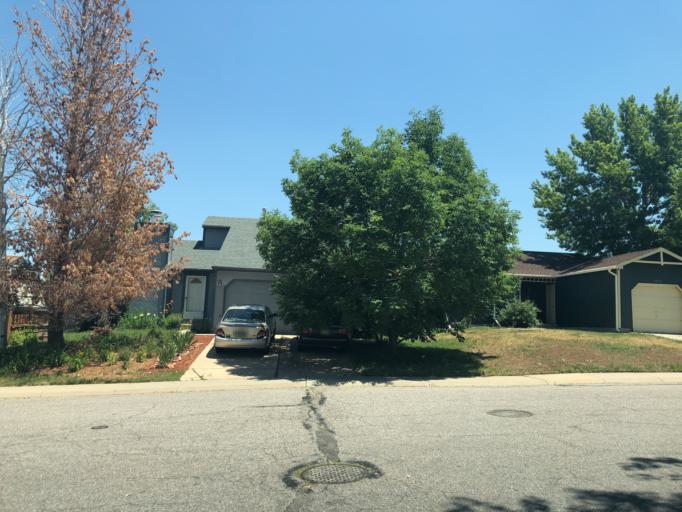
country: US
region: Colorado
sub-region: Arapahoe County
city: Dove Valley
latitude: 39.6270
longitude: -104.7576
